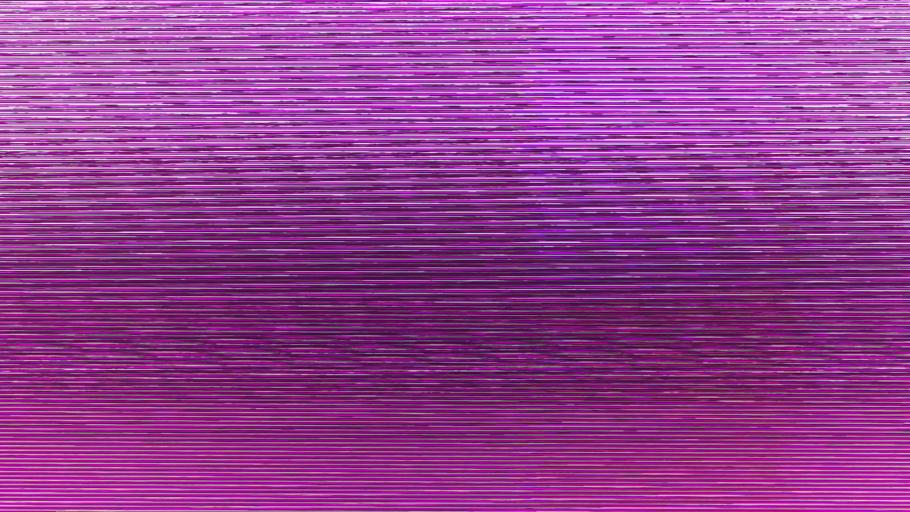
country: US
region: Michigan
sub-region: Genesee County
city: Flint
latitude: 43.0054
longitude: -83.7243
